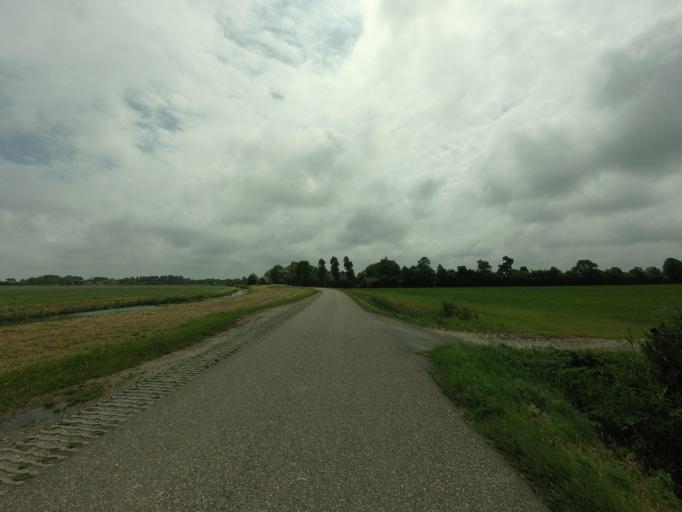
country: NL
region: North Holland
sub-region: Gemeente Schagen
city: Schagen
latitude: 52.7921
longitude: 4.7676
